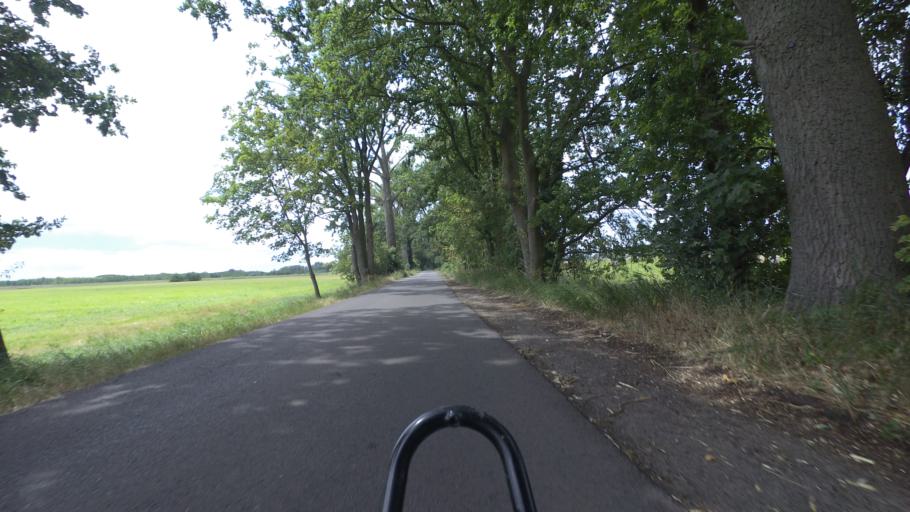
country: DE
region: Brandenburg
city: Trebbin
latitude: 52.2388
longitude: 13.1210
